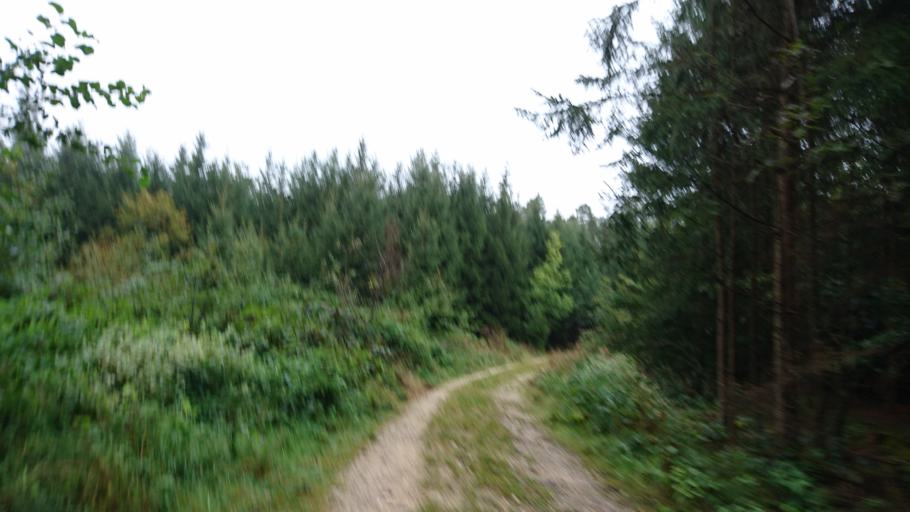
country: DE
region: Bavaria
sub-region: Swabia
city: Welden
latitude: 48.4489
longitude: 10.6483
